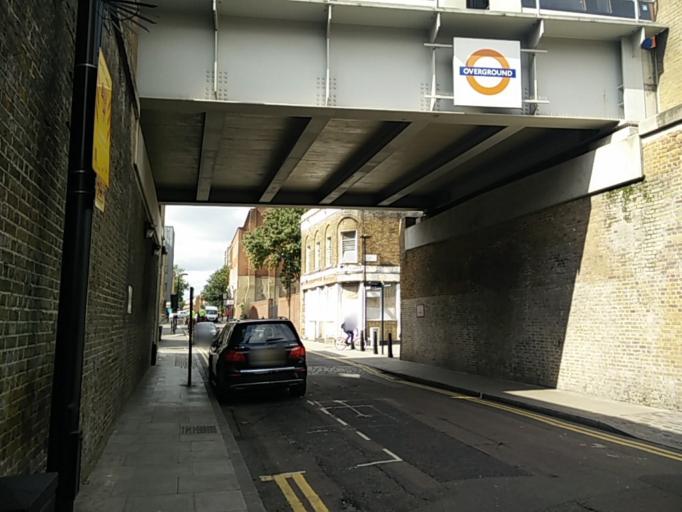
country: GB
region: England
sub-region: Greater London
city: Bethnal Green
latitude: 51.5307
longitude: -0.0755
